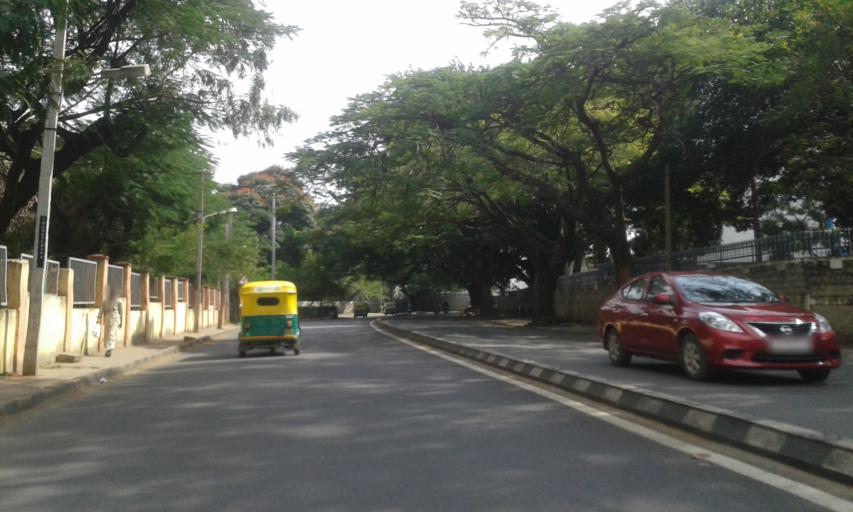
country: IN
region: Karnataka
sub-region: Bangalore Urban
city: Bangalore
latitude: 12.9658
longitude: 77.6258
